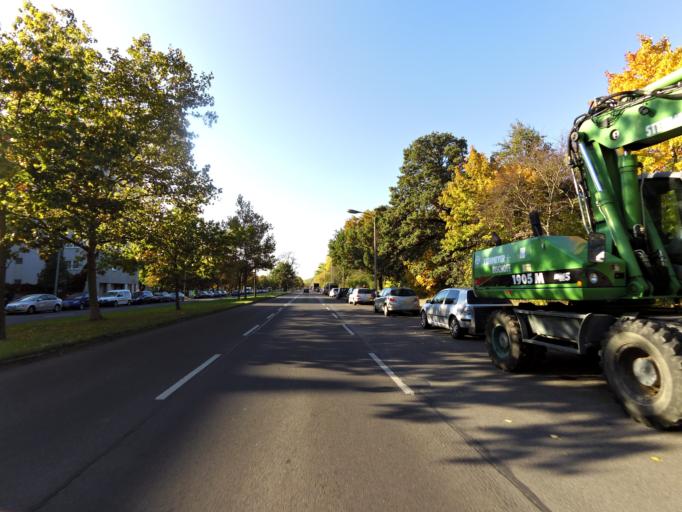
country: DE
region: Berlin
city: Oberschoneweide
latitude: 52.4637
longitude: 13.5282
